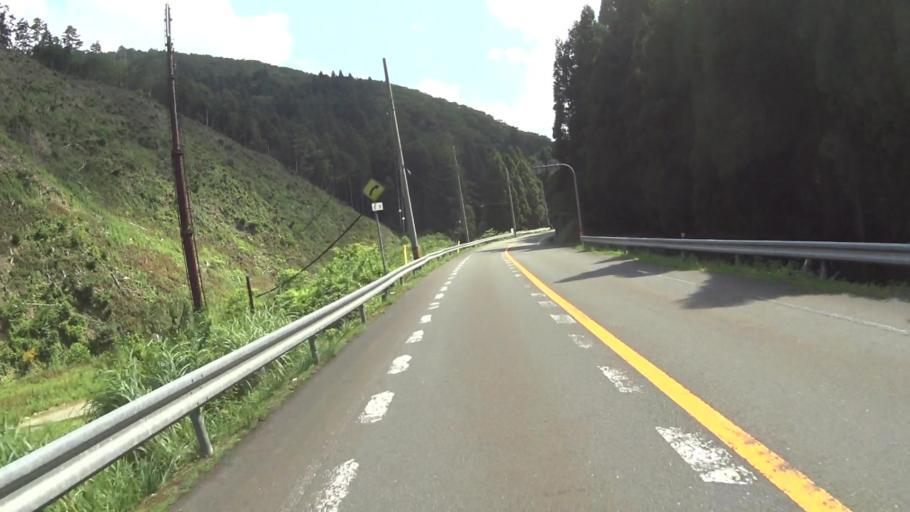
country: JP
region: Fukui
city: Obama
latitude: 35.3564
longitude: 135.5974
